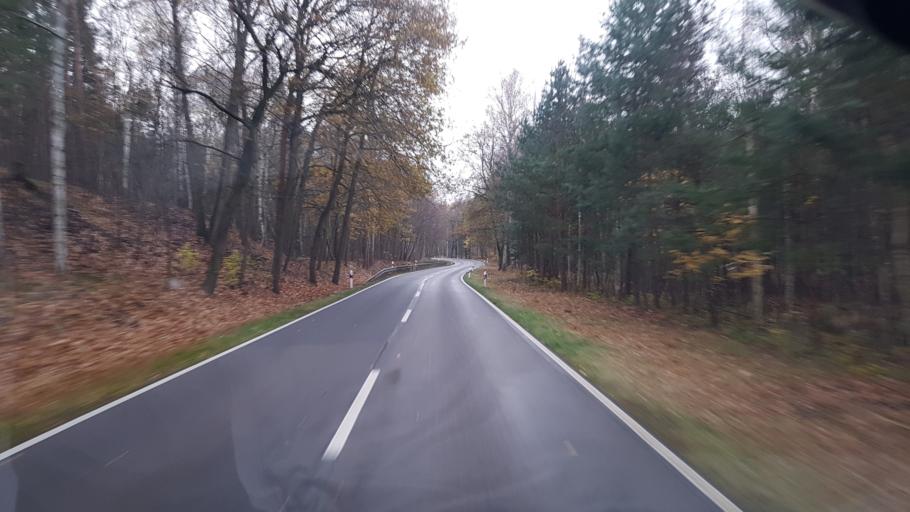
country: DE
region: Brandenburg
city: Lauchhammer
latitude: 51.5028
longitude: 13.7231
